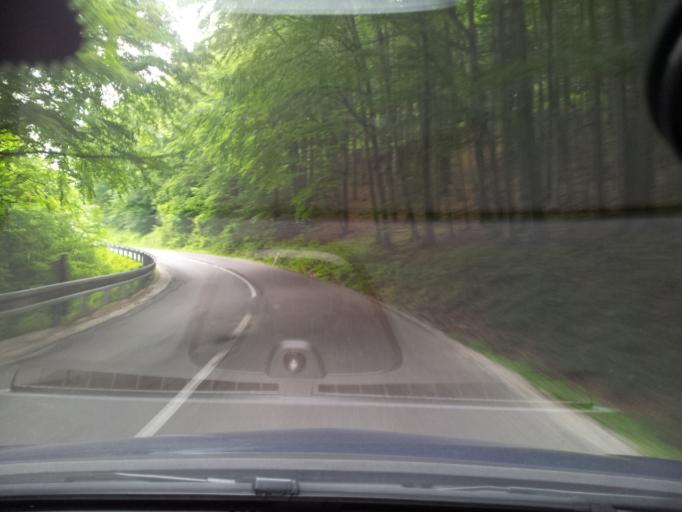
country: SK
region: Nitriansky
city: Partizanske
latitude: 48.5372
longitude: 18.4455
